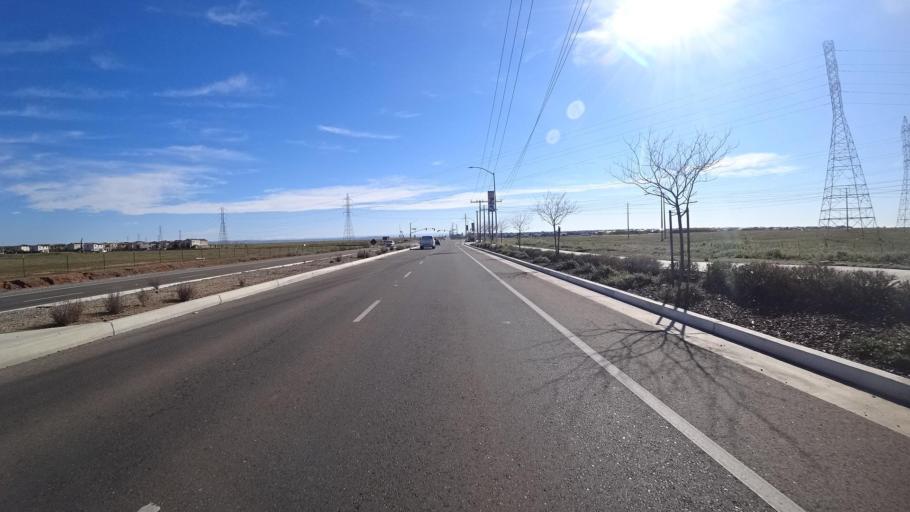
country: US
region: California
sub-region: Sacramento County
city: Gold River
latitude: 38.5598
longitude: -121.2049
